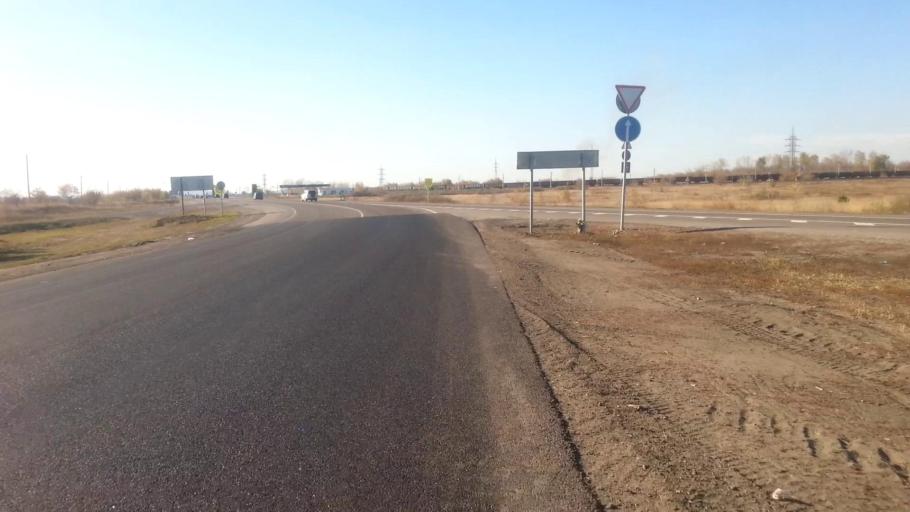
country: RU
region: Altai Krai
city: Novoaltaysk
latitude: 53.3728
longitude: 83.9520
